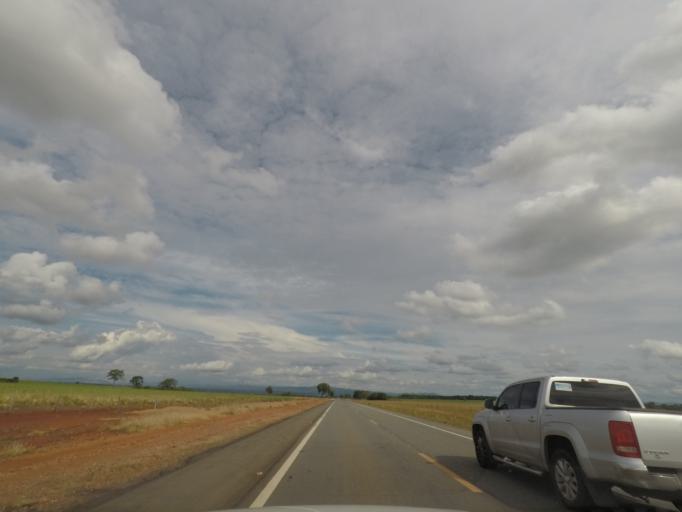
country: BR
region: Goias
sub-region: Uruacu
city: Uruacu
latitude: -14.6939
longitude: -49.1171
